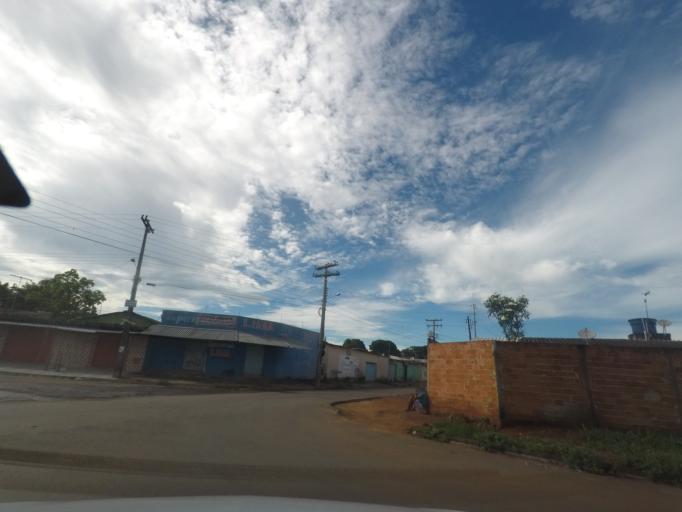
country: BR
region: Goias
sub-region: Aparecida De Goiania
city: Aparecida de Goiania
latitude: -16.8294
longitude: -49.2983
